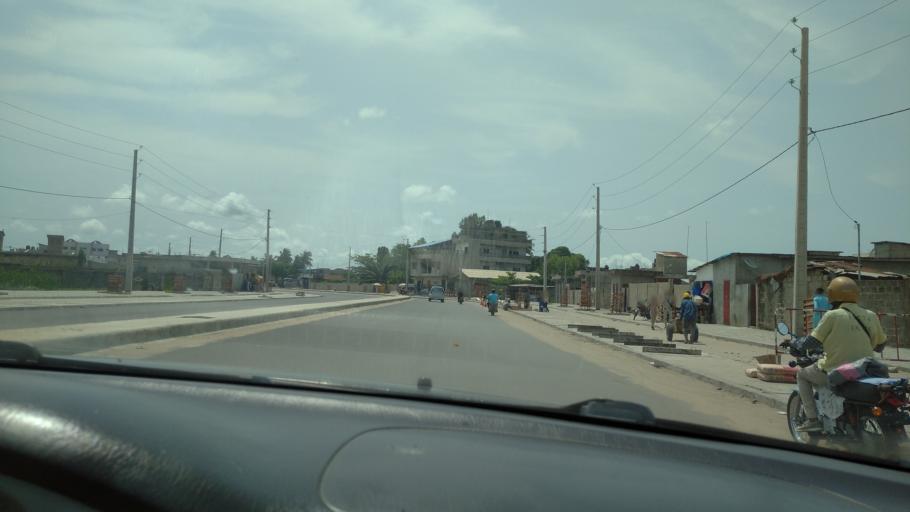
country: BJ
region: Littoral
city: Cotonou
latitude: 6.3737
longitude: 2.4974
